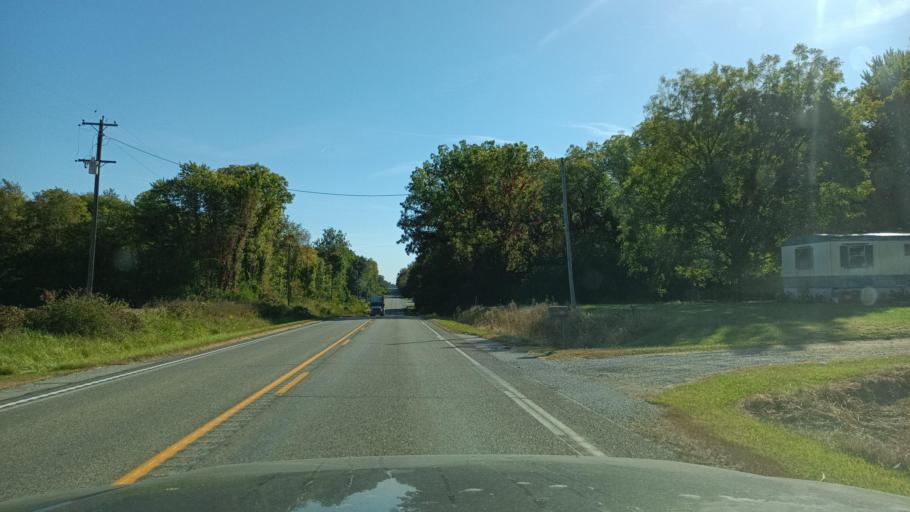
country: US
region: Indiana
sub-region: Vigo County
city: Seelyville
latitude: 39.3903
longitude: -87.2661
